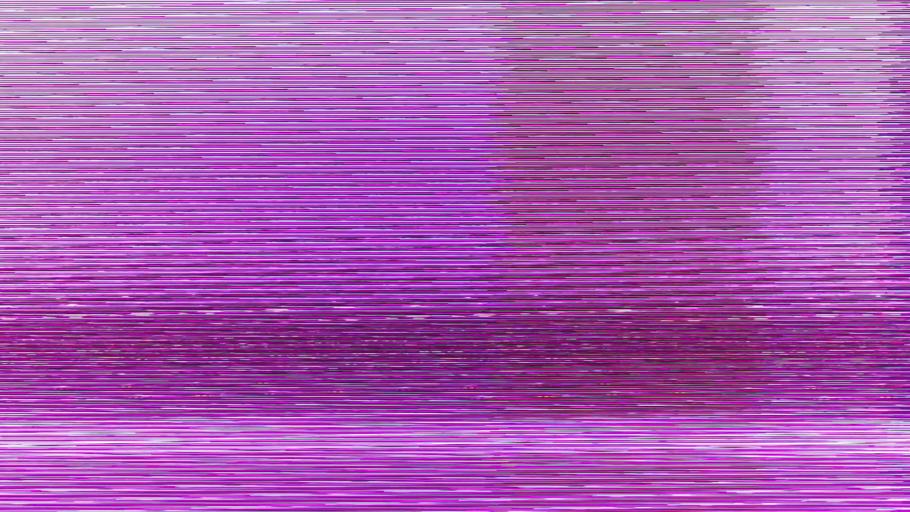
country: US
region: Michigan
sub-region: Livingston County
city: Brighton
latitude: 42.5357
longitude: -83.7836
